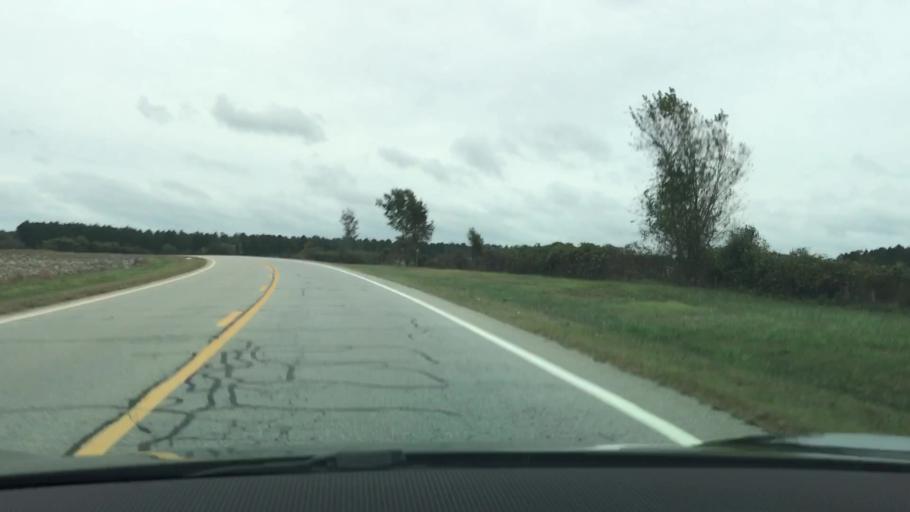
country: US
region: Georgia
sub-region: Warren County
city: Warrenton
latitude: 33.3579
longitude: -82.5952
